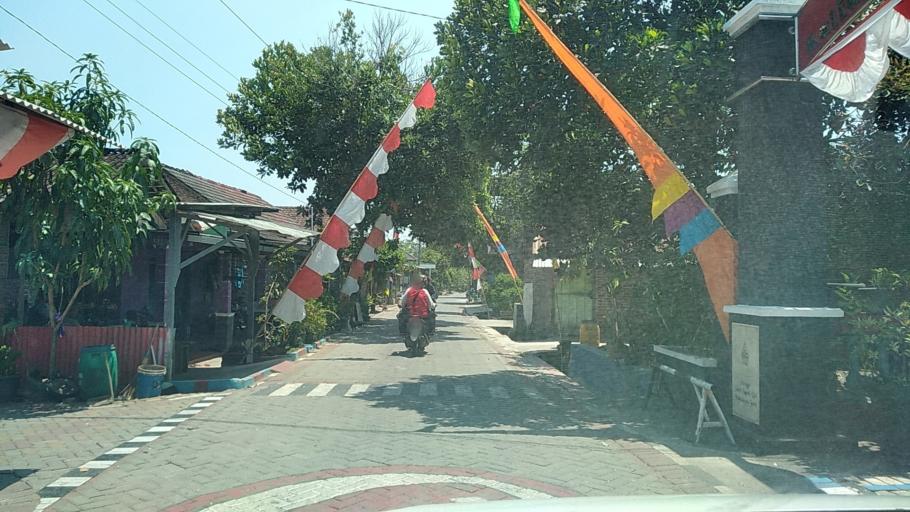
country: ID
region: Central Java
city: Semarang
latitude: -7.0292
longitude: 110.3782
